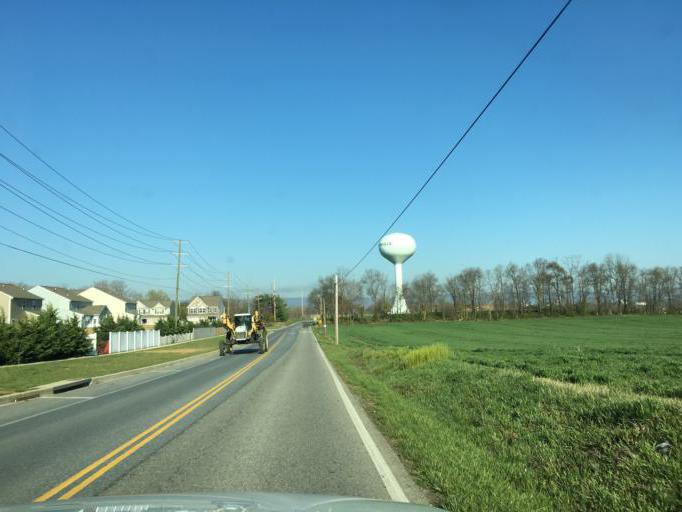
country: US
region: Maryland
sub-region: Frederick County
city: Walkersville
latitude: 39.4954
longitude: -77.3431
